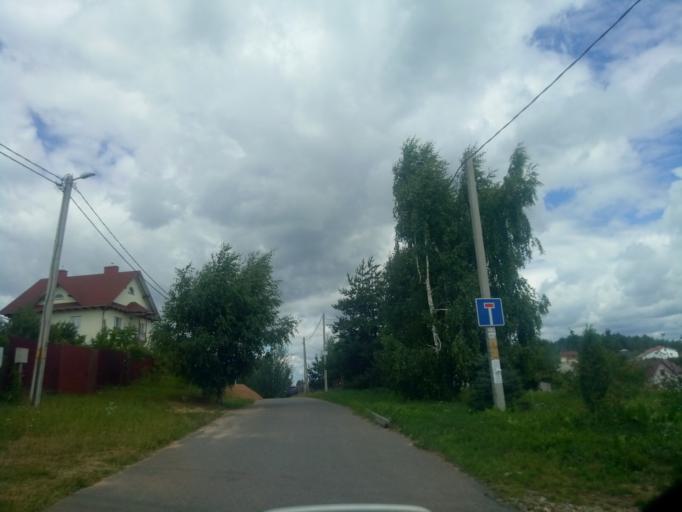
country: BY
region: Minsk
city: Zhdanovichy
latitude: 53.9403
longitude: 27.4022
